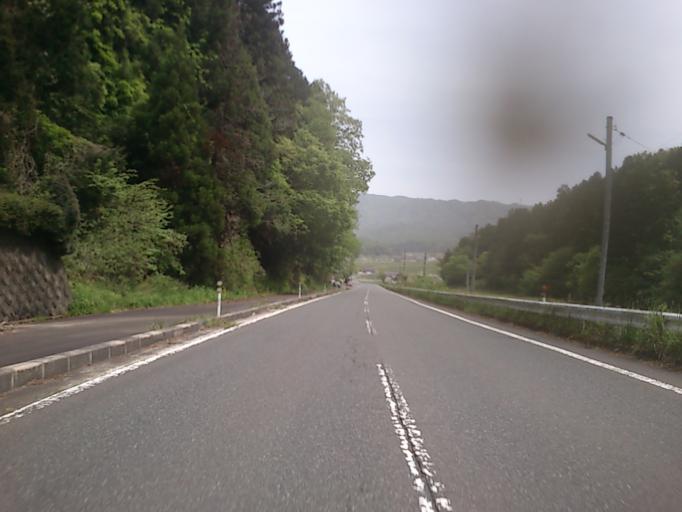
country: JP
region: Kyoto
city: Miyazu
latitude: 35.5888
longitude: 135.1277
